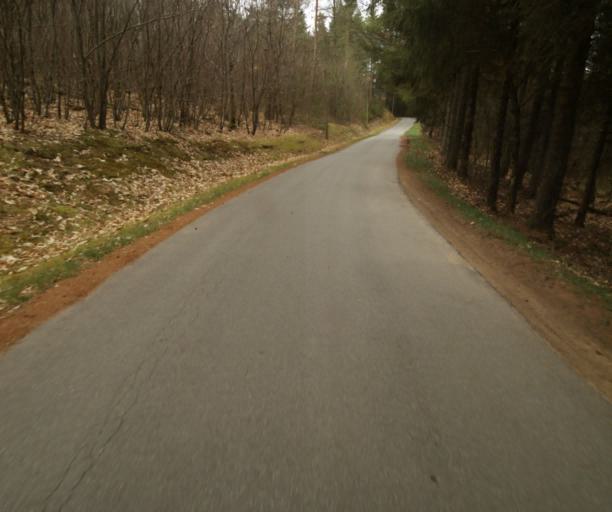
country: FR
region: Limousin
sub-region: Departement de la Correze
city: Correze
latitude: 45.3191
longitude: 1.9508
